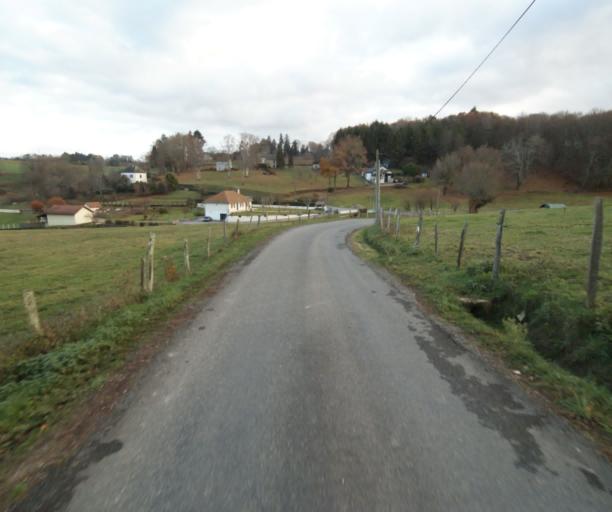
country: FR
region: Limousin
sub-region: Departement de la Correze
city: Laguenne
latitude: 45.2313
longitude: 1.7707
